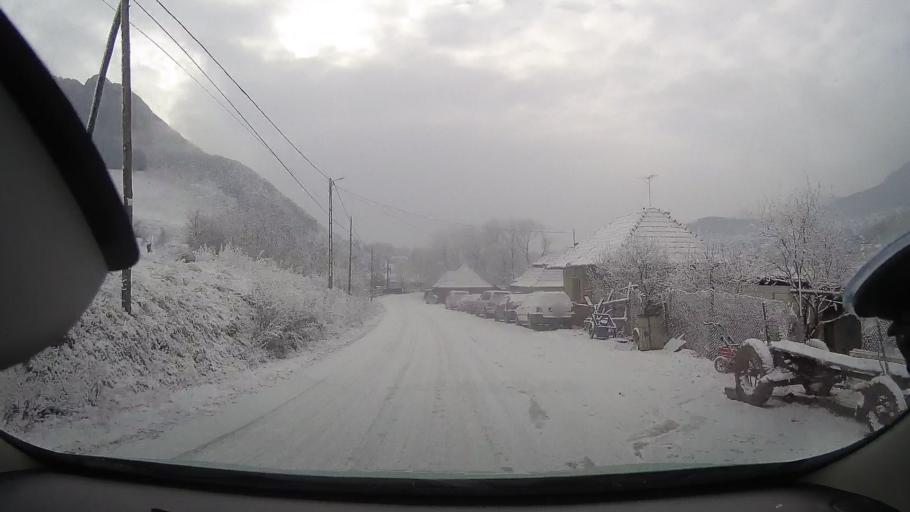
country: RO
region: Alba
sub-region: Comuna Rimetea
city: Rimetea
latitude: 46.4599
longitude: 23.5715
